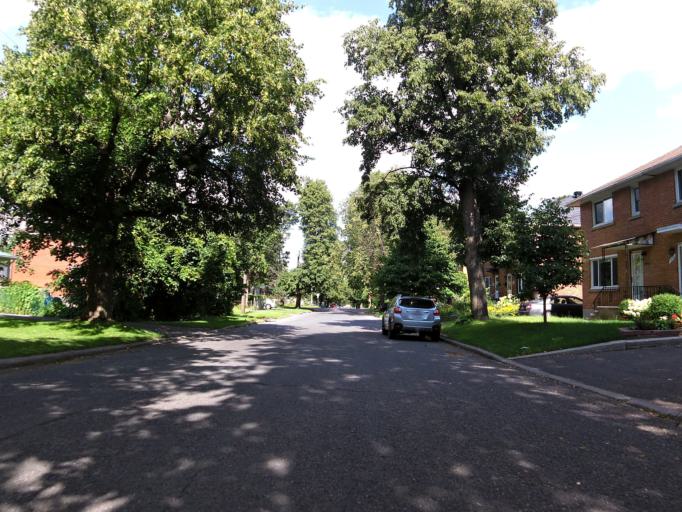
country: CA
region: Ontario
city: Ottawa
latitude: 45.3752
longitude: -75.7313
